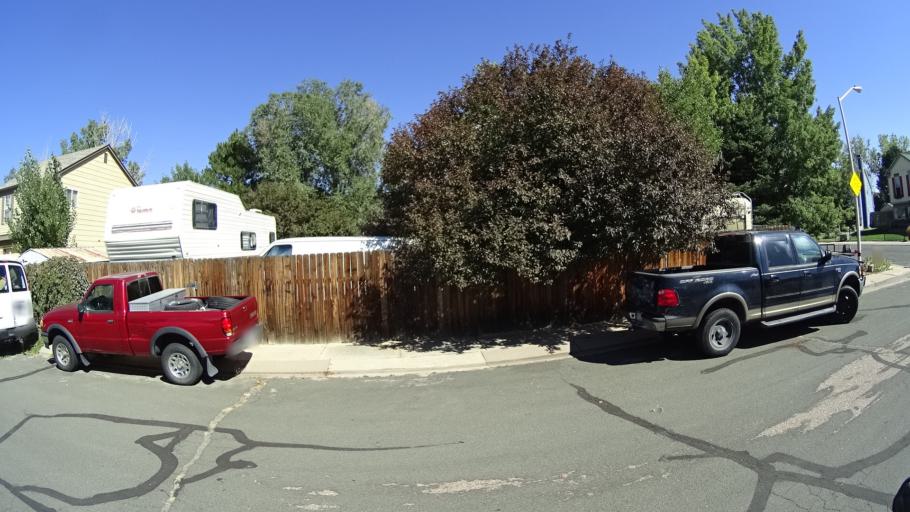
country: US
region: Colorado
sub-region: El Paso County
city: Stratmoor
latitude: 38.7950
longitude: -104.7368
